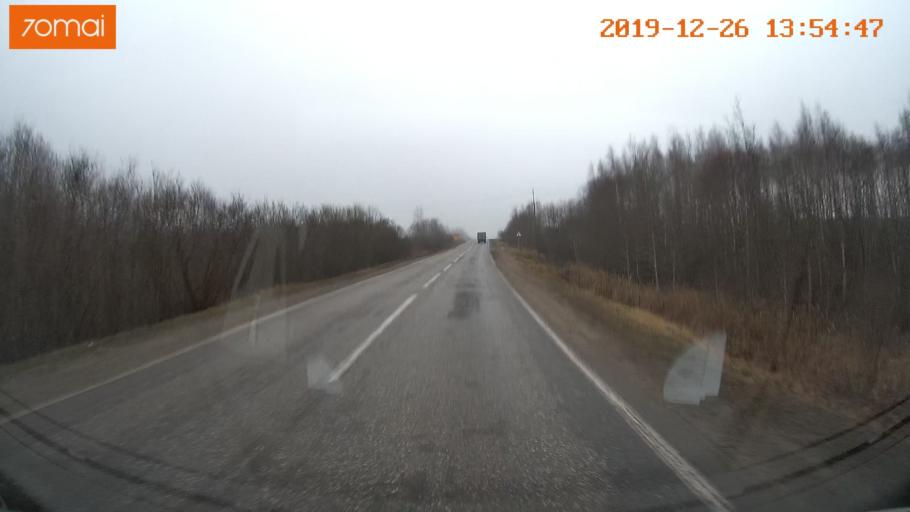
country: RU
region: Jaroslavl
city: Poshekhon'ye
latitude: 58.6101
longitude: 38.6395
